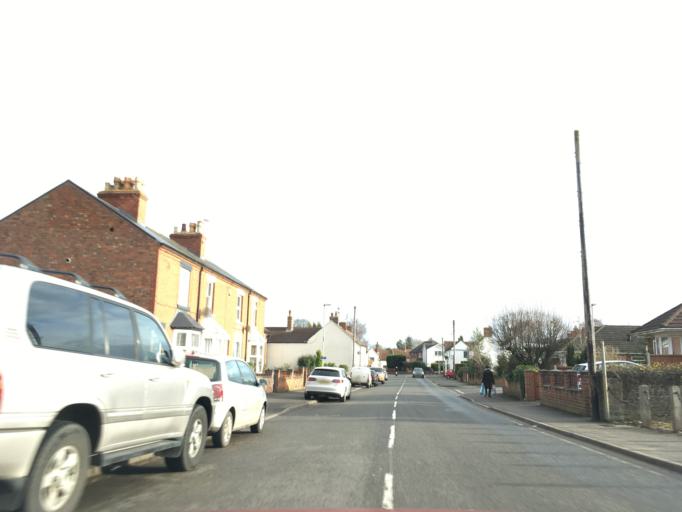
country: GB
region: England
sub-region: Nottinghamshire
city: East Leake
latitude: 52.8313
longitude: -1.1750
